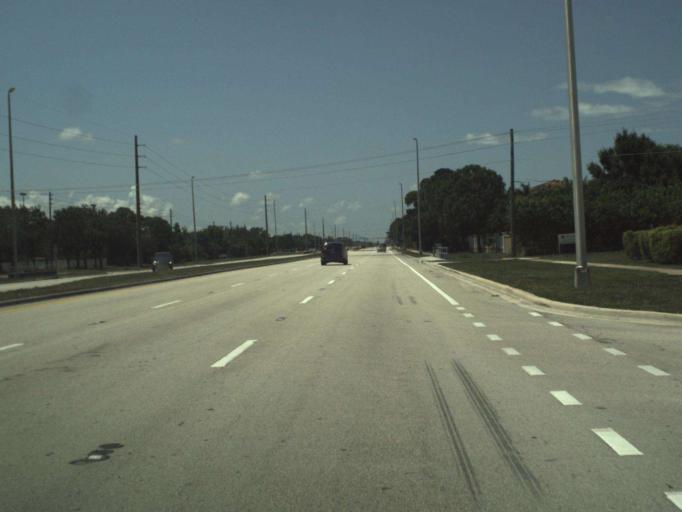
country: US
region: Florida
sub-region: Saint Lucie County
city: Port Saint Lucie
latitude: 27.2814
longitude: -80.2942
